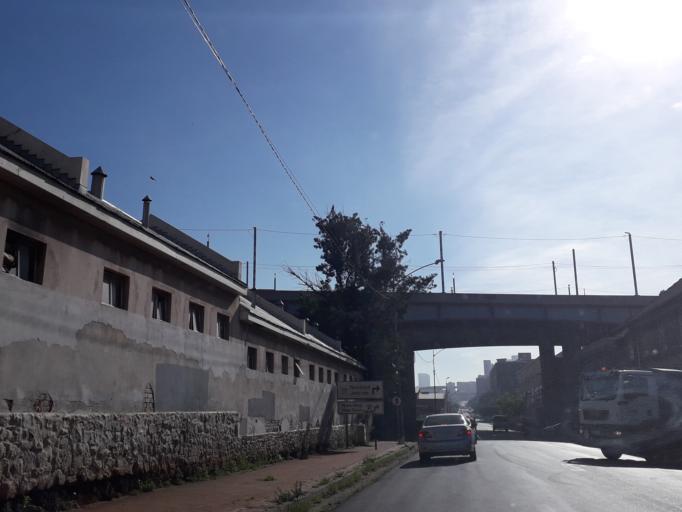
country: ZA
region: Gauteng
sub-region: City of Johannesburg Metropolitan Municipality
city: Johannesburg
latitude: -26.2002
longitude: 28.0290
